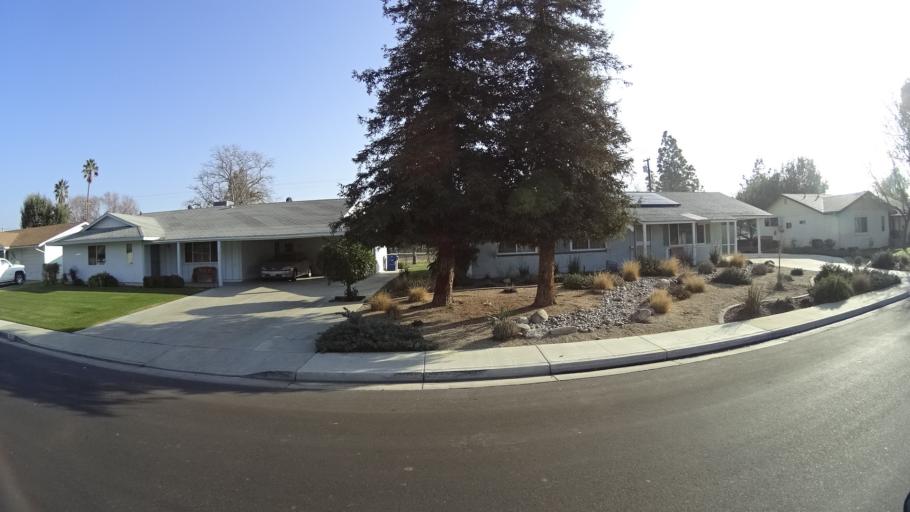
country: US
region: California
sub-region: Kern County
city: Bakersfield
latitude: 35.3467
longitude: -119.0667
